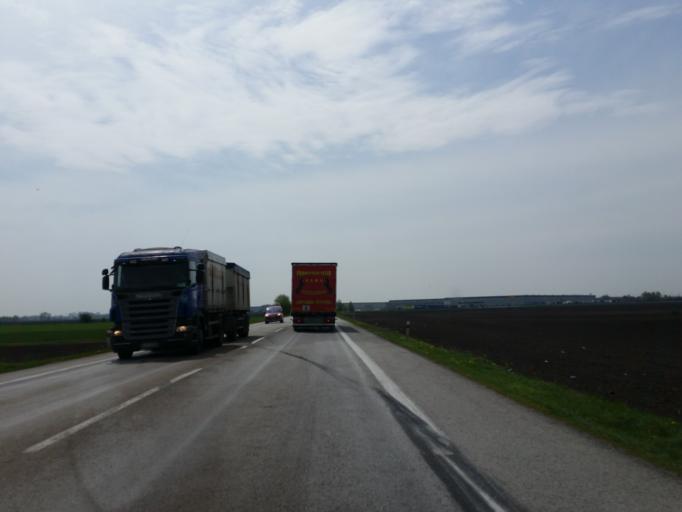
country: SK
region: Trnavsky
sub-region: Okres Galanta
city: Galanta
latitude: 48.2440
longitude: 17.7364
